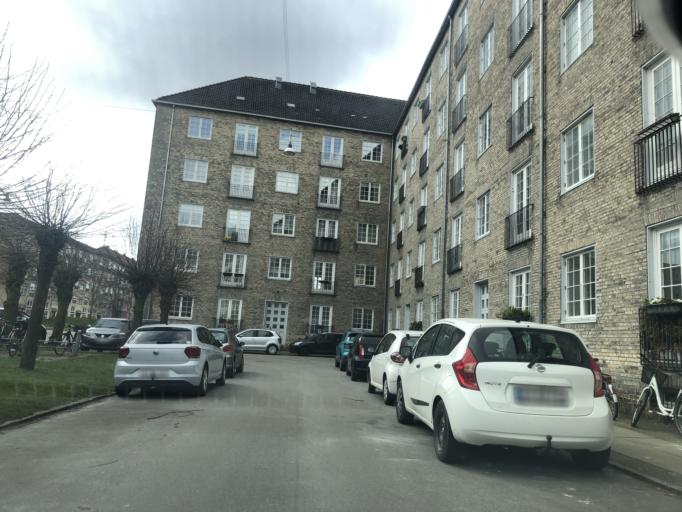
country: DK
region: Capital Region
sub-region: Kobenhavn
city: Christianshavn
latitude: 55.6548
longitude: 12.6016
